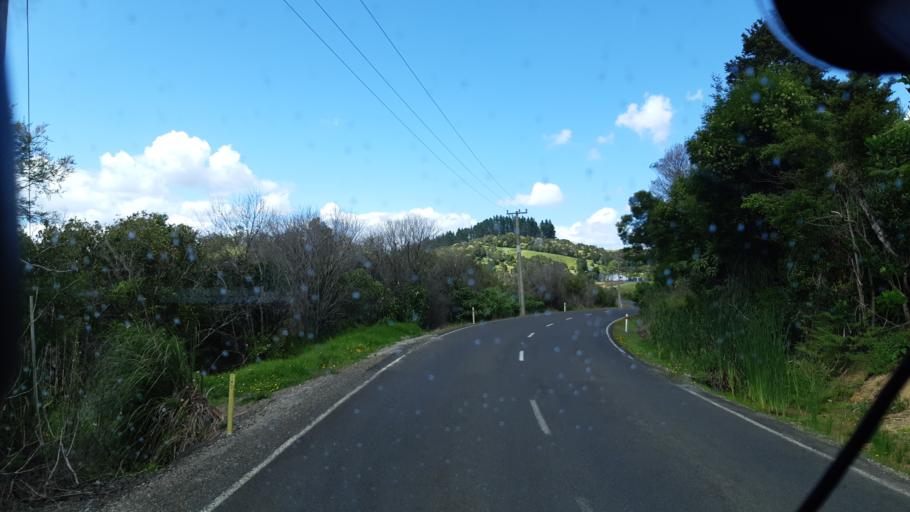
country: NZ
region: Northland
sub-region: Far North District
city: Taipa
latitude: -35.2708
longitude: 173.5227
